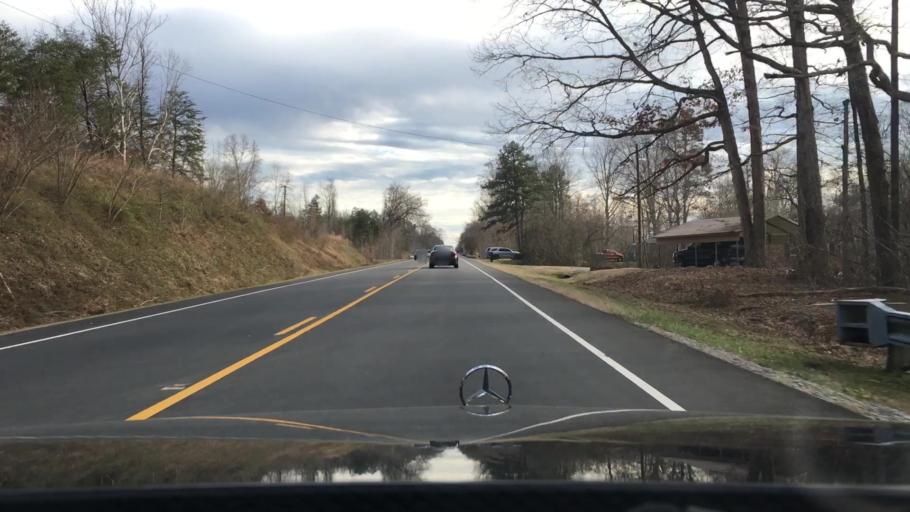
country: US
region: North Carolina
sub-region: Caswell County
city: Yanceyville
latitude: 36.4601
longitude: -79.3718
